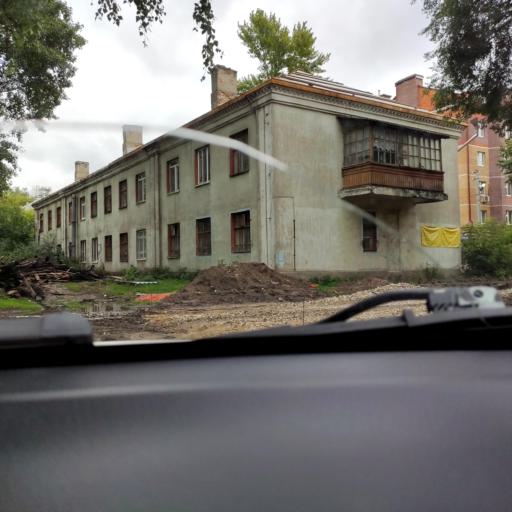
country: RU
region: Tatarstan
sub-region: Gorod Kazan'
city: Kazan
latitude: 55.8405
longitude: 49.0624
